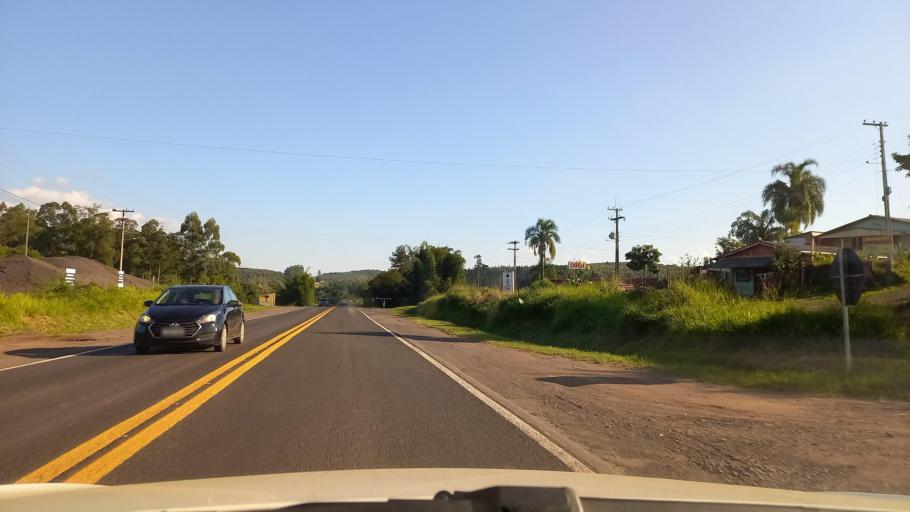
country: BR
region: Rio Grande do Sul
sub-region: Taquari
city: Taquari
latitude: -29.6967
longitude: -51.7493
